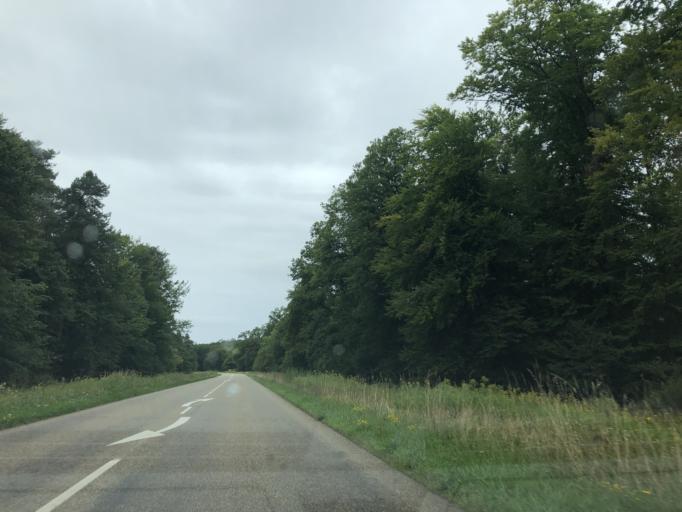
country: DE
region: Rheinland-Pfalz
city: Scheibenhardt
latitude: 48.9850
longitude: 8.1090
